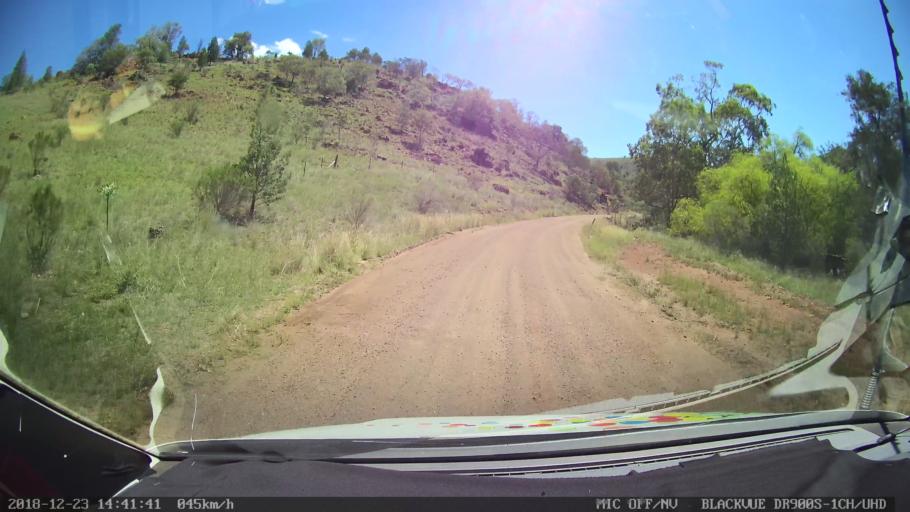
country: AU
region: New South Wales
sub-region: Tamworth Municipality
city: Manilla
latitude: -30.6330
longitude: 150.9012
